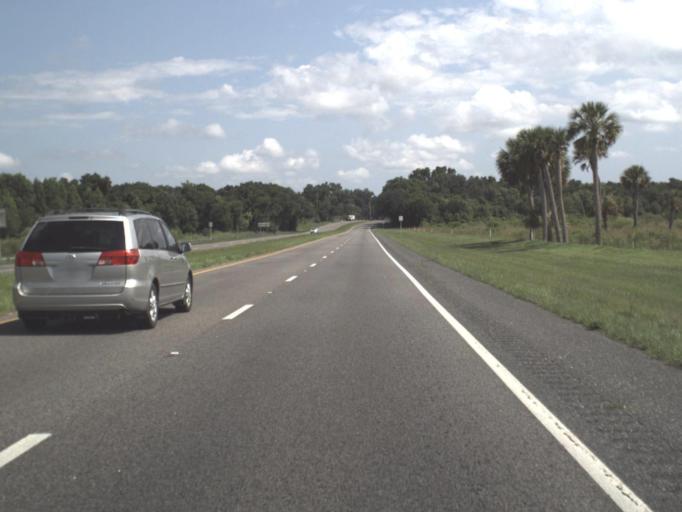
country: US
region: Florida
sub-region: Alachua County
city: Gainesville
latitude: 29.5840
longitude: -82.3377
